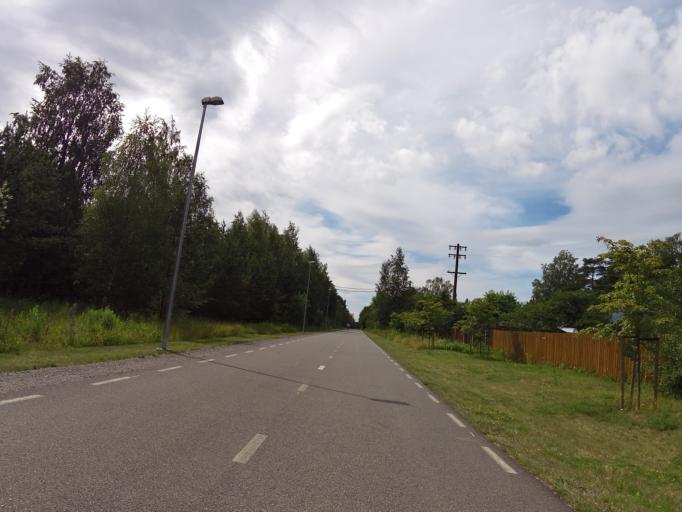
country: EE
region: Harju
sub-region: Saue vald
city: Laagri
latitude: 59.3831
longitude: 24.6548
